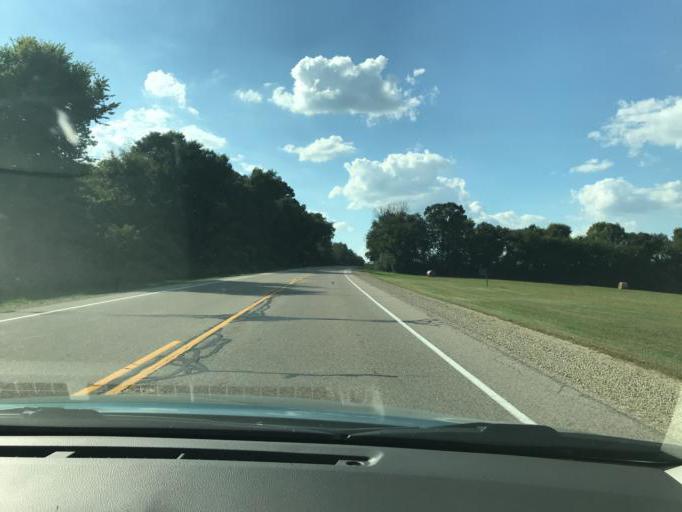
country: US
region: Wisconsin
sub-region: Rock County
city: Orfordville
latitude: 42.5260
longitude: -89.2213
